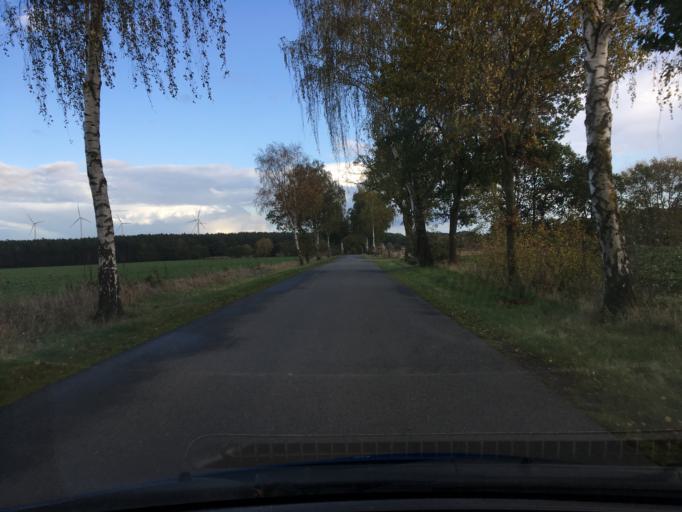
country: DE
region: Lower Saxony
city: Barendorf
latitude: 53.2506
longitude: 10.5441
